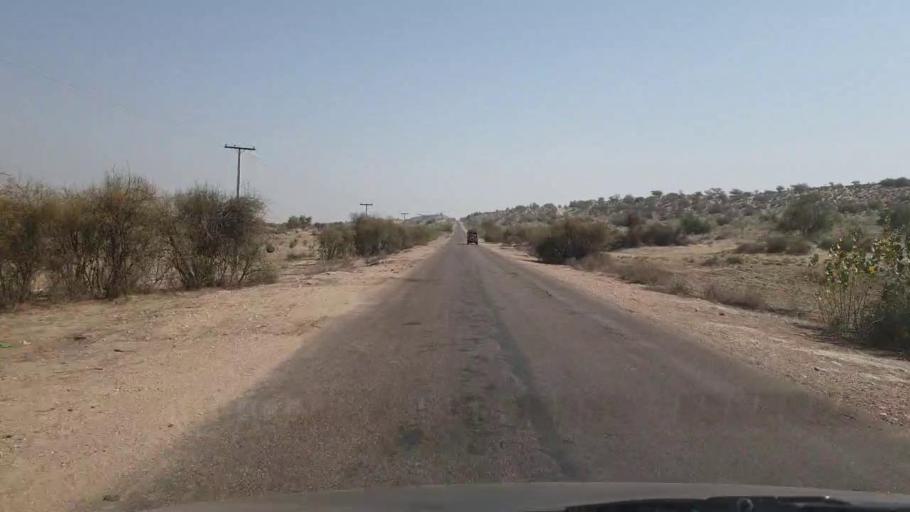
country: PK
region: Sindh
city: Chor
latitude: 25.5778
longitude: 69.9176
